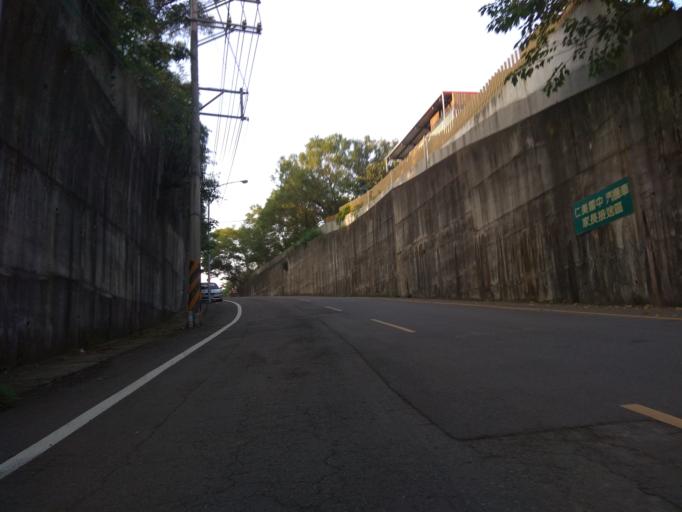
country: TW
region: Taiwan
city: Daxi
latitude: 24.9240
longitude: 121.1830
